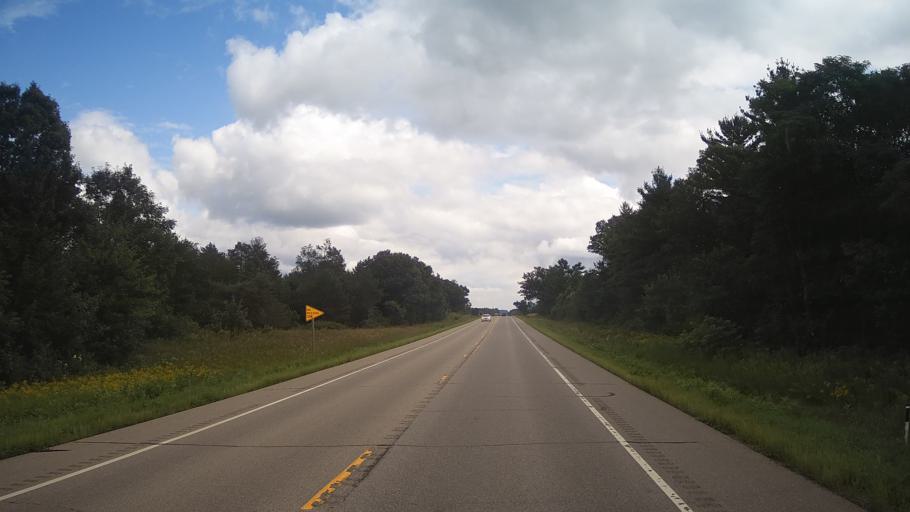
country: US
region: Wisconsin
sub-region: Adams County
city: Friendship
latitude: 44.0220
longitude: -89.6441
